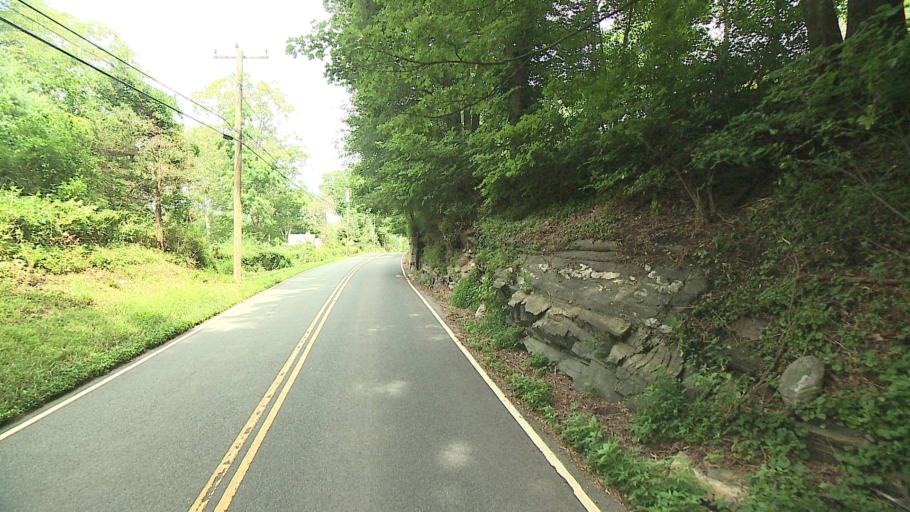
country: US
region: Connecticut
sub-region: Litchfield County
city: New Milford
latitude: 41.5812
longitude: -73.3204
